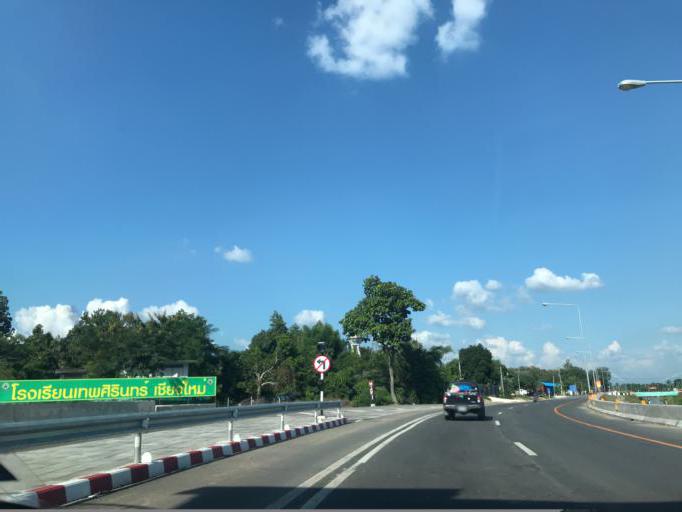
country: TH
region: Chiang Mai
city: San Pa Tong
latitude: 18.6453
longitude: 98.8488
